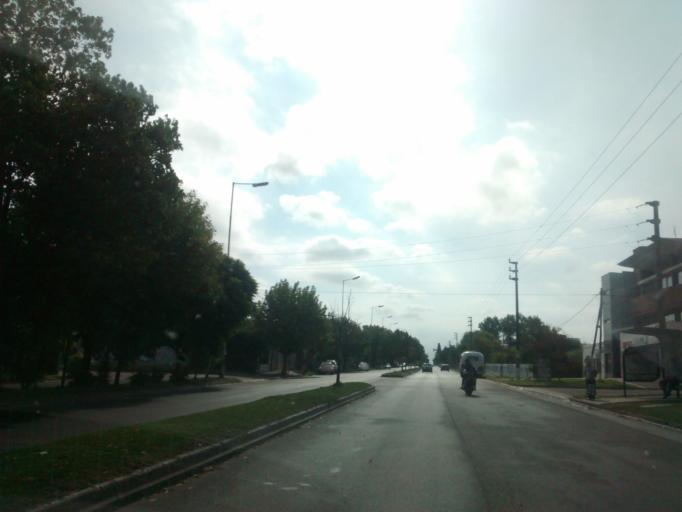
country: AR
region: Buenos Aires
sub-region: Partido de La Plata
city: La Plata
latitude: -34.9400
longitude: -57.9158
